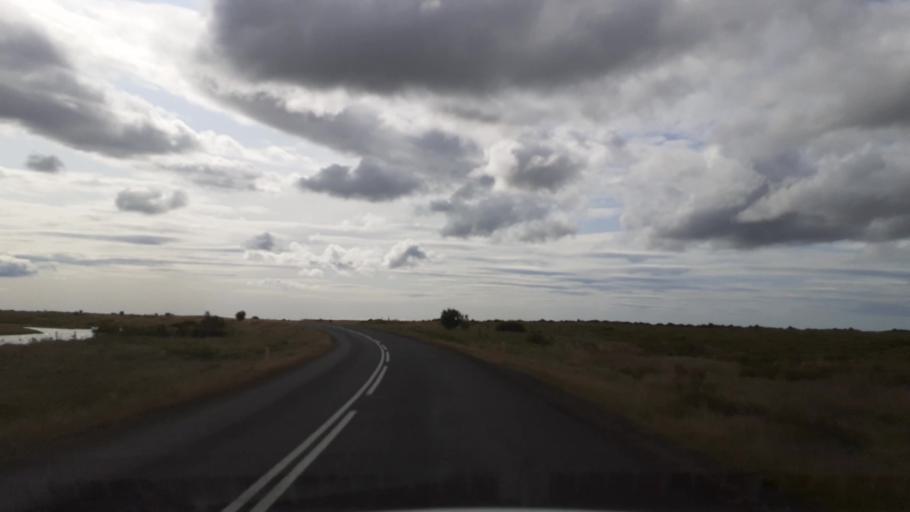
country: IS
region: South
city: Vestmannaeyjar
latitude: 63.8263
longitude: -20.4279
